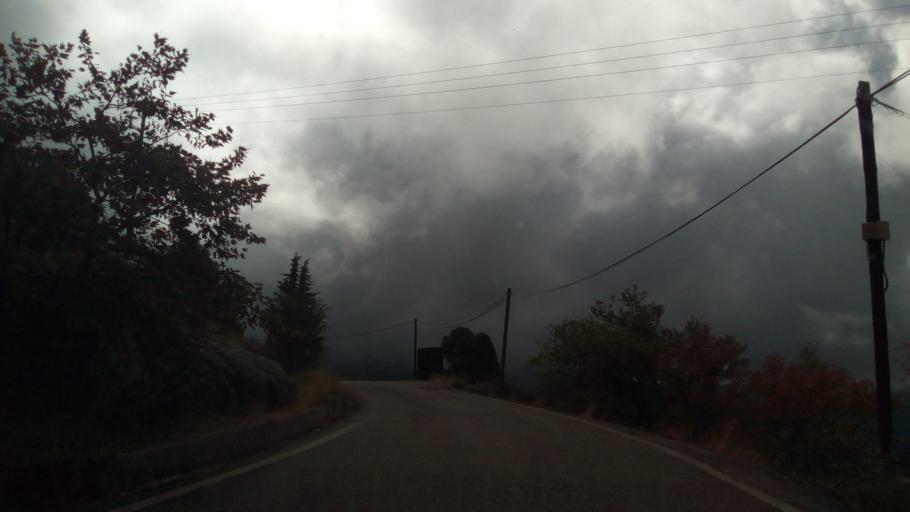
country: GR
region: West Greece
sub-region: Nomos Aitolias kai Akarnanias
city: Nafpaktos
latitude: 38.5286
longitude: 21.8322
